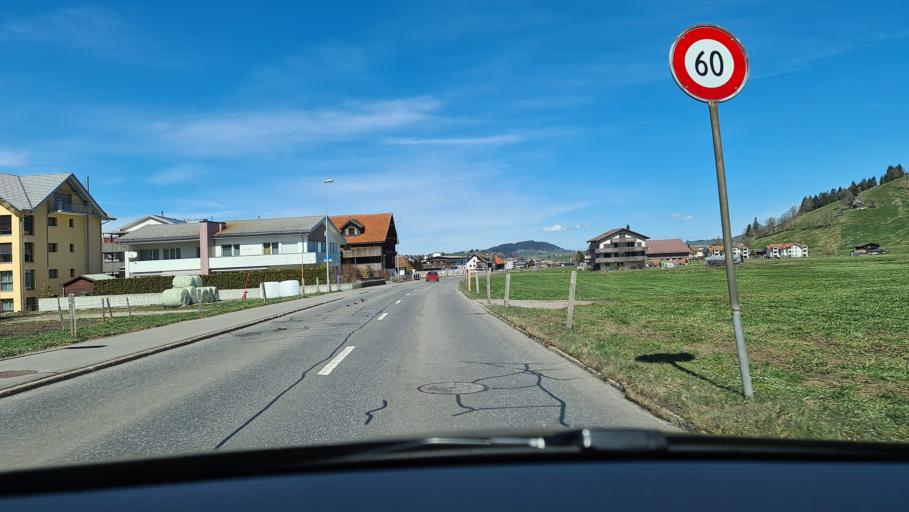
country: CH
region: Schwyz
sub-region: Bezirk Einsiedeln
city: Einsiedeln
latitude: 47.1131
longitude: 8.7359
